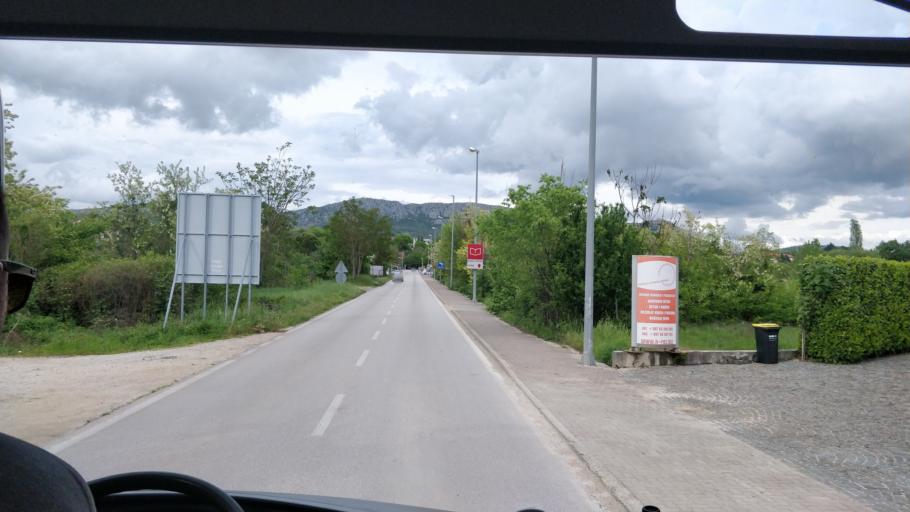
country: BA
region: Federation of Bosnia and Herzegovina
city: Ljubuski
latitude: 43.1814
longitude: 17.5208
